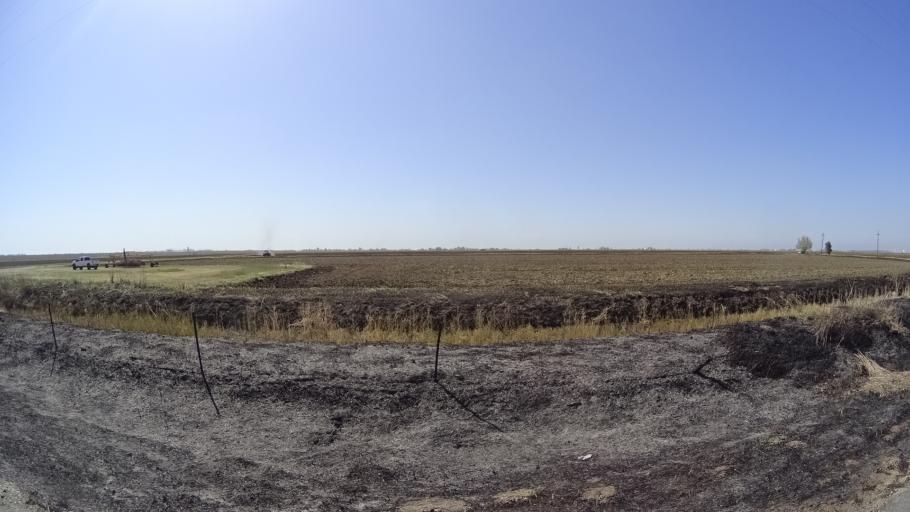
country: US
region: California
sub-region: Glenn County
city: Willows
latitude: 39.4812
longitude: -122.0404
